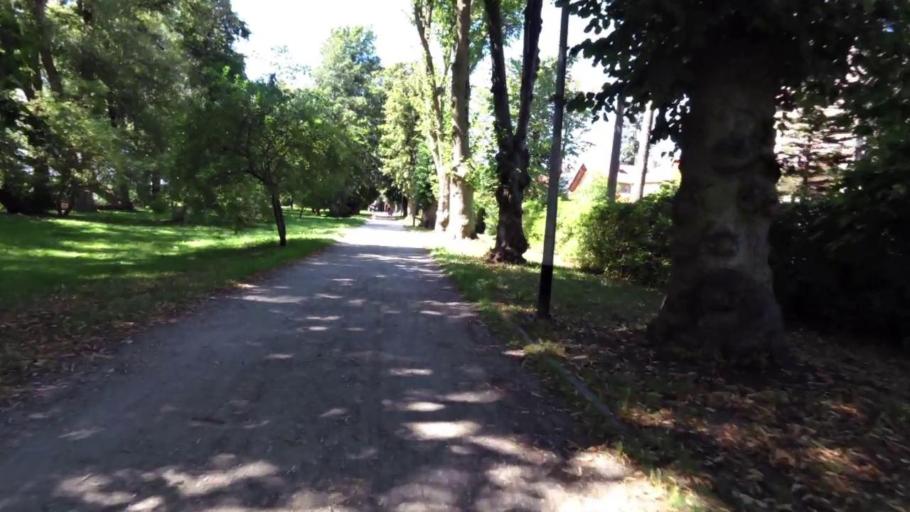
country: PL
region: West Pomeranian Voivodeship
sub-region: Powiat szczecinecki
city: Szczecinek
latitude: 53.7139
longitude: 16.6745
